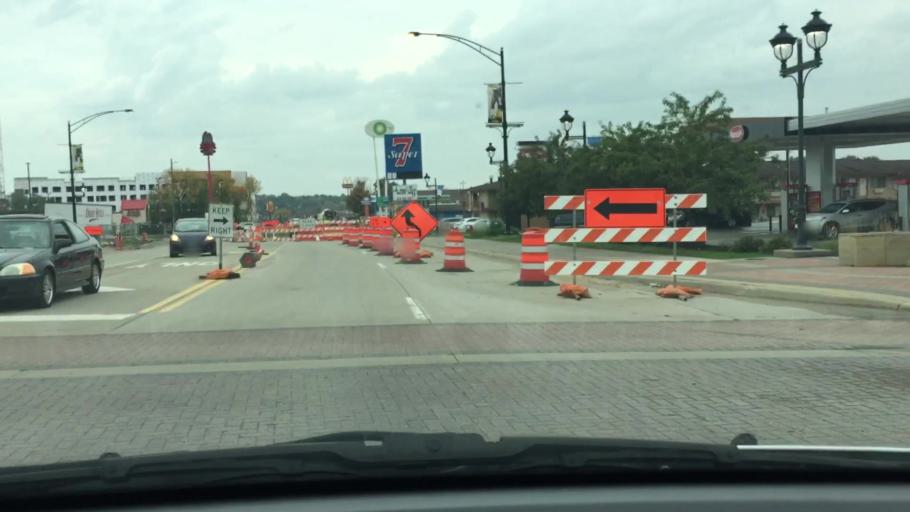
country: US
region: Iowa
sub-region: Johnson County
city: Coralville
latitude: 41.6816
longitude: -91.5659
